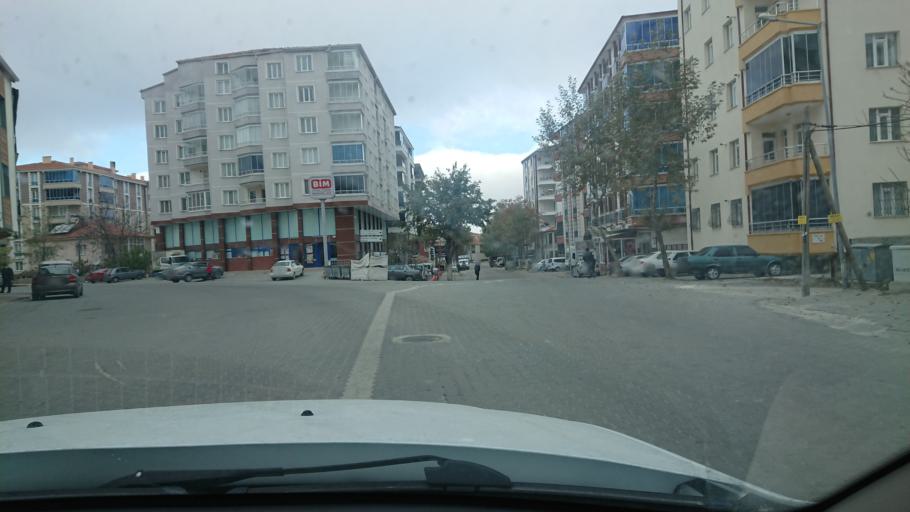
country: TR
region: Aksaray
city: Ortakoy
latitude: 38.7388
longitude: 34.0385
